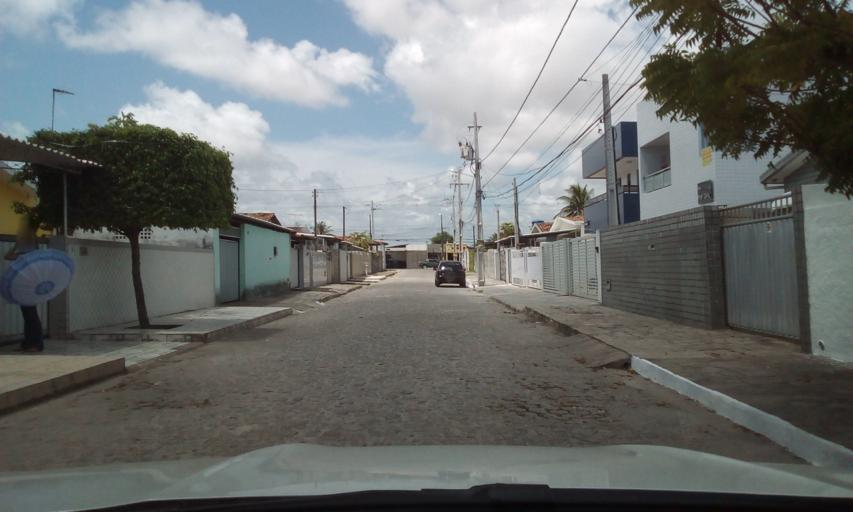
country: BR
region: Paraiba
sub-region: Joao Pessoa
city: Joao Pessoa
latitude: -7.1676
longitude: -34.8413
